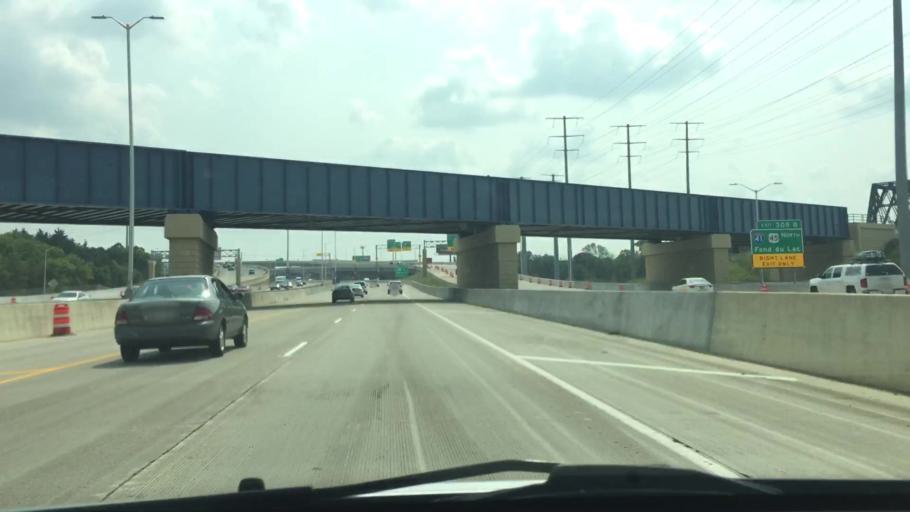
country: US
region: Wisconsin
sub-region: Waukesha County
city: Elm Grove
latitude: 43.0278
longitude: -88.0466
